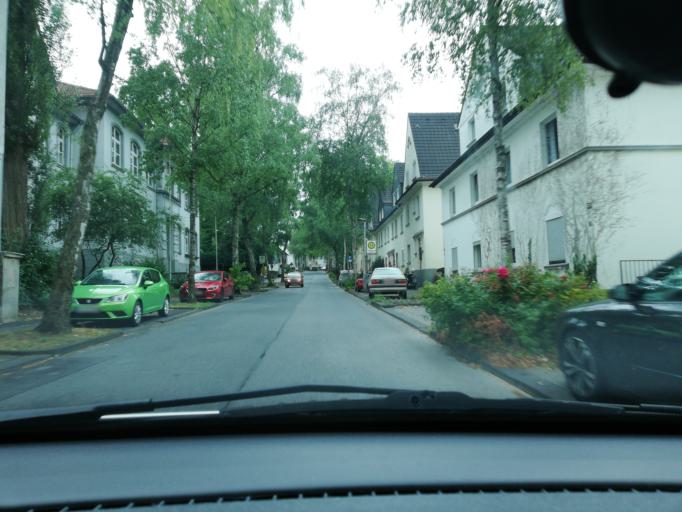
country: DE
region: North Rhine-Westphalia
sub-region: Regierungsbezirk Dusseldorf
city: Solingen
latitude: 51.1756
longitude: 7.0985
